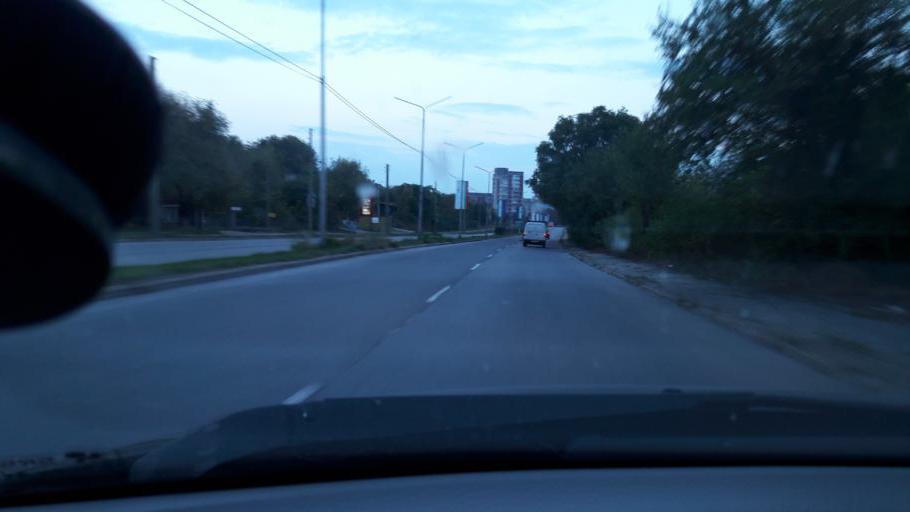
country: BG
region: Razgrad
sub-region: Obshtina Razgrad
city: Razgrad
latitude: 43.5376
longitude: 26.5193
